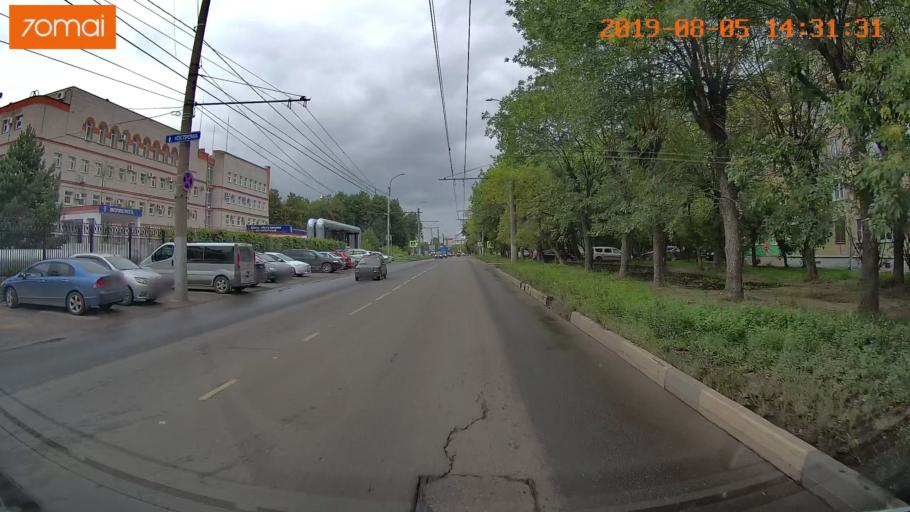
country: RU
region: Ivanovo
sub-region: Gorod Ivanovo
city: Ivanovo
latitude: 56.9872
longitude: 41.0011
